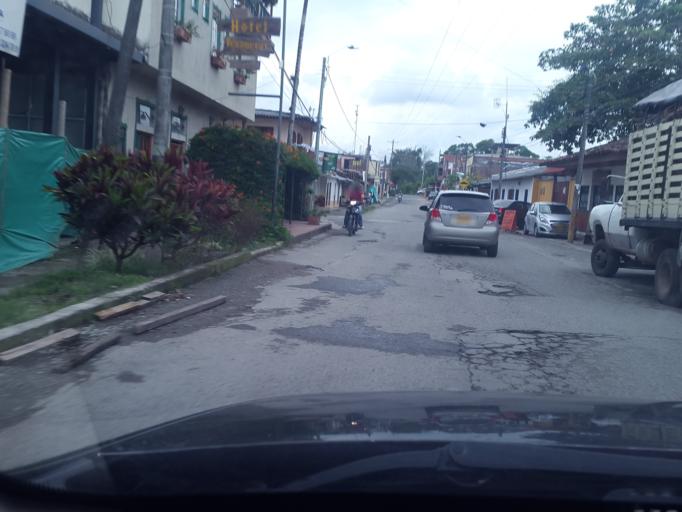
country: CO
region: Quindio
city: La Tebaida
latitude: 4.5106
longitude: -75.7856
